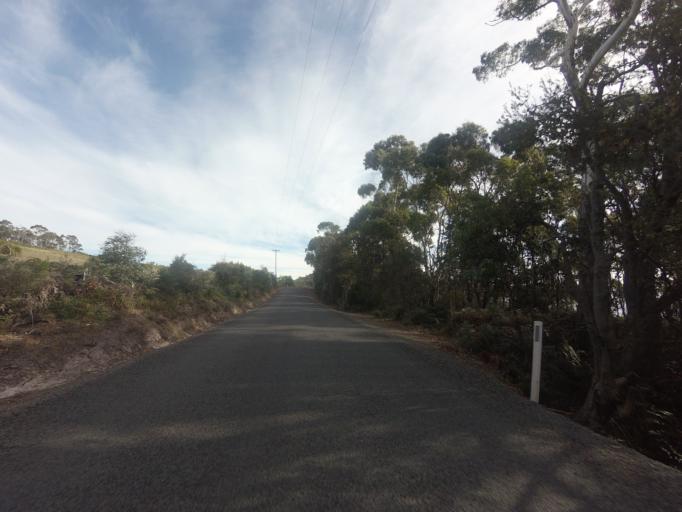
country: AU
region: Tasmania
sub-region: Sorell
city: Sorell
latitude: -42.9627
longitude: 147.8362
